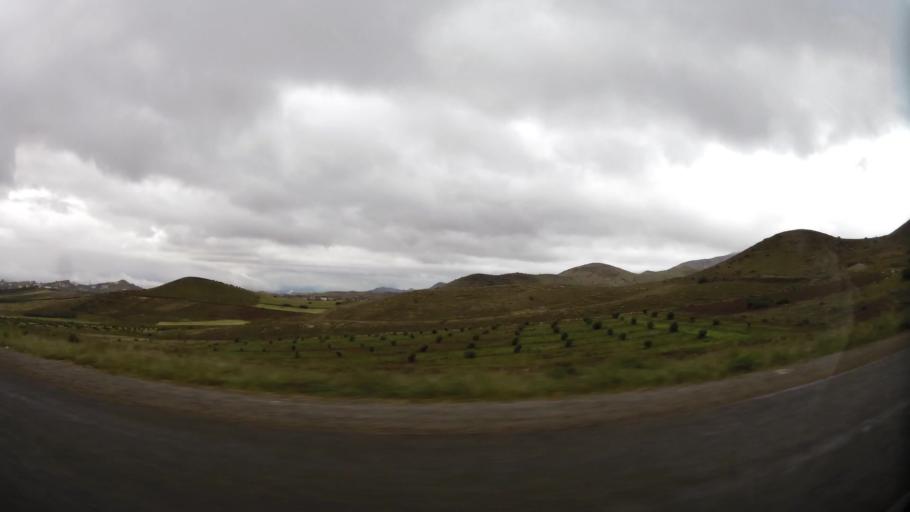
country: MA
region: Oriental
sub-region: Nador
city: Midar
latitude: 35.0663
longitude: -3.4746
